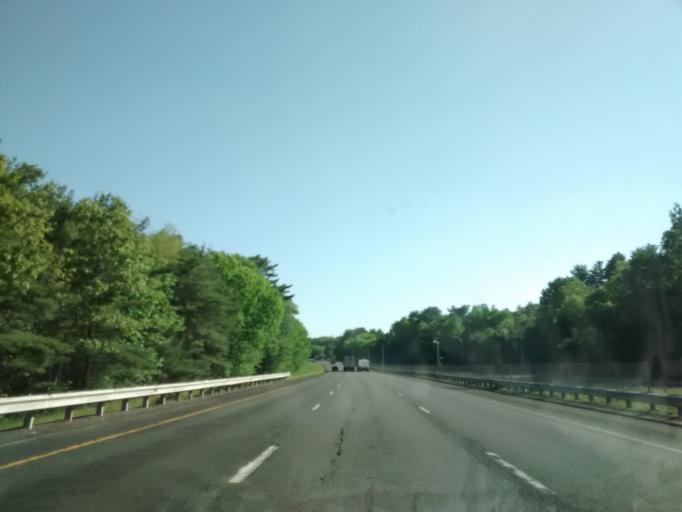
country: US
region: Massachusetts
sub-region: Hampden County
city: Holland
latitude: 42.0525
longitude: -72.1199
